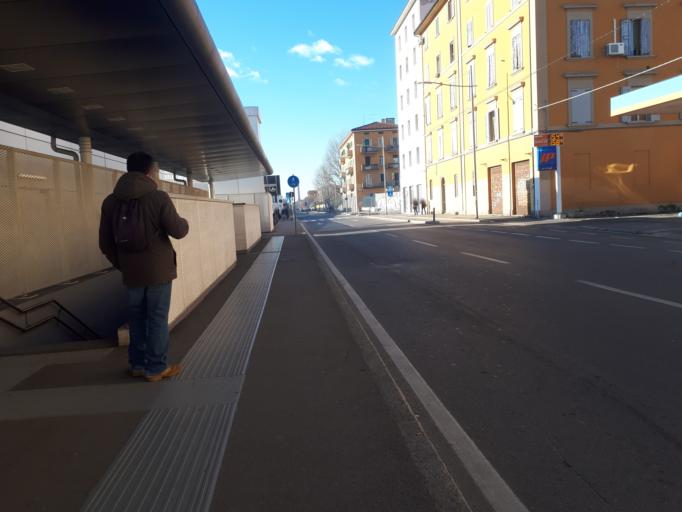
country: IT
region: Emilia-Romagna
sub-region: Provincia di Bologna
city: Bologna
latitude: 44.5075
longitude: 11.3411
